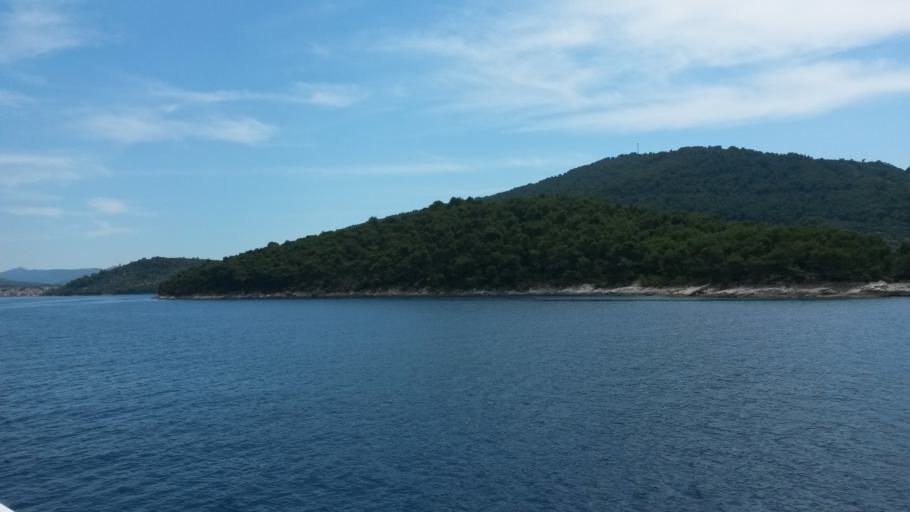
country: HR
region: Dubrovacko-Neretvanska
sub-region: Grad Dubrovnik
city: Vela Luka
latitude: 42.9643
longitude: 16.6765
